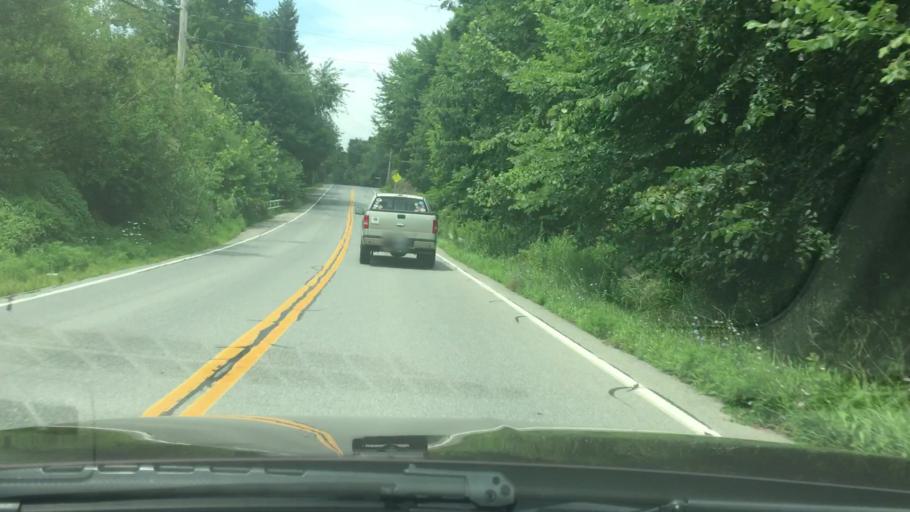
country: US
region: New York
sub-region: Dutchess County
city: Hillside Lake
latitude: 41.6517
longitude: -73.7527
